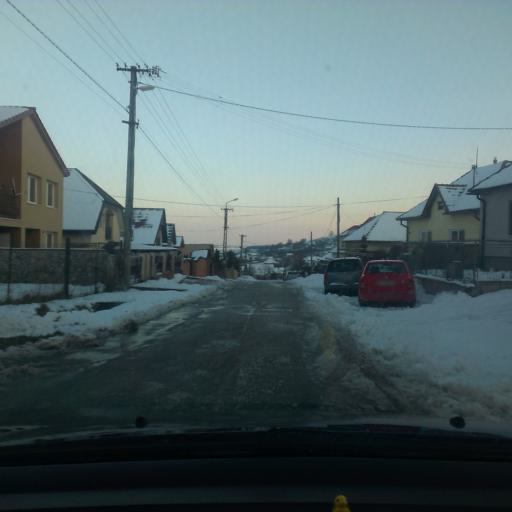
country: SK
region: Nitriansky
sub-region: Okres Nitra
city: Nitra
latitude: 48.3782
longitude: 18.1723
